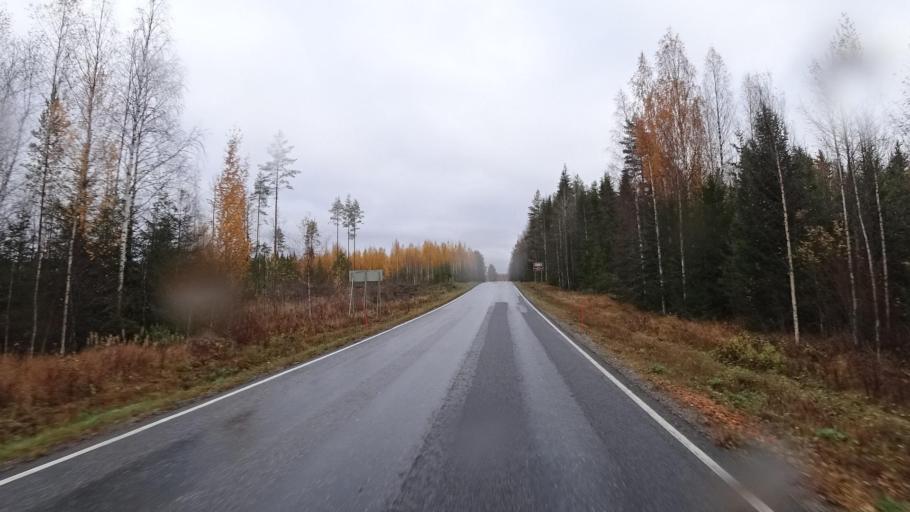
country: FI
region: North Karelia
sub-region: Joensuu
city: Polvijaervi
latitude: 63.0912
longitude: 29.6012
